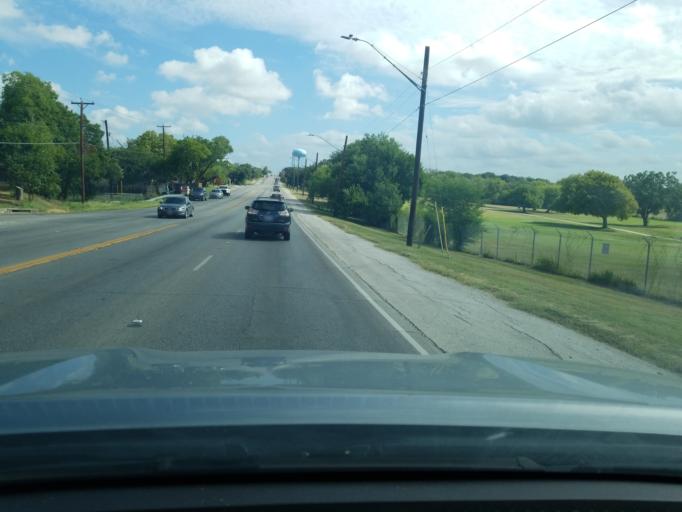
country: US
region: Texas
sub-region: Bexar County
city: Terrell Hills
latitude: 29.4723
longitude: -98.4368
